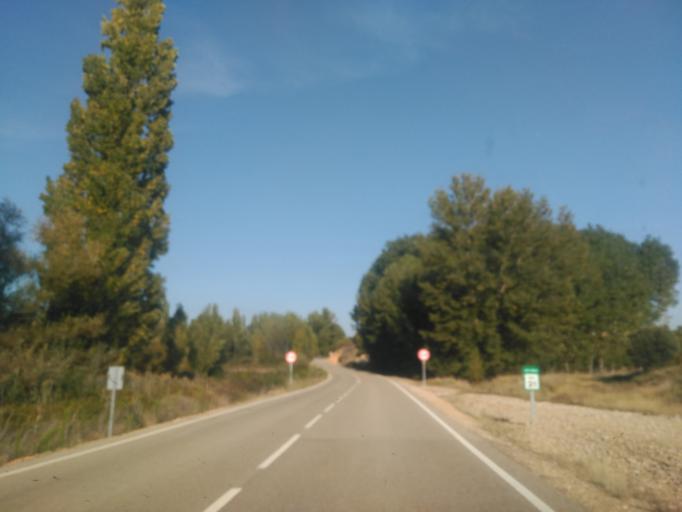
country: ES
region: Castille and Leon
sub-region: Provincia de Soria
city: Alcubilla de Avellaneda
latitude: 41.7546
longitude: -3.2697
